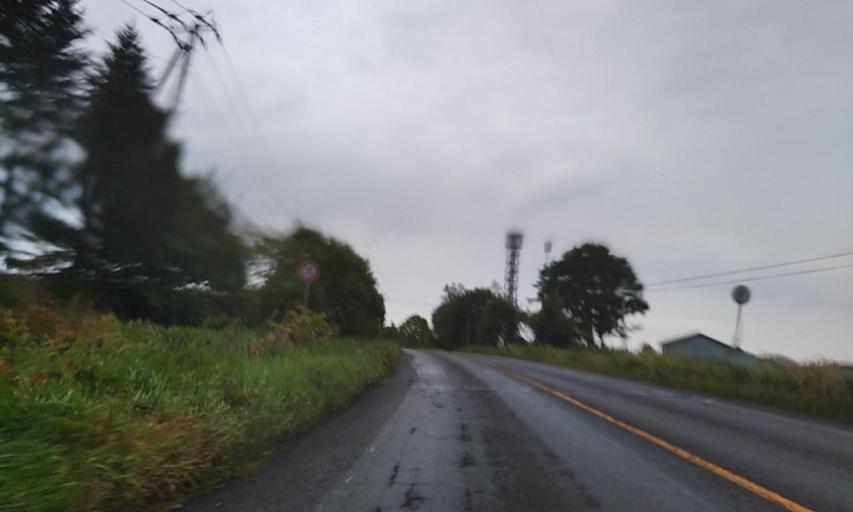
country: JP
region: Hokkaido
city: Mombetsu
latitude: 44.4825
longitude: 143.0977
